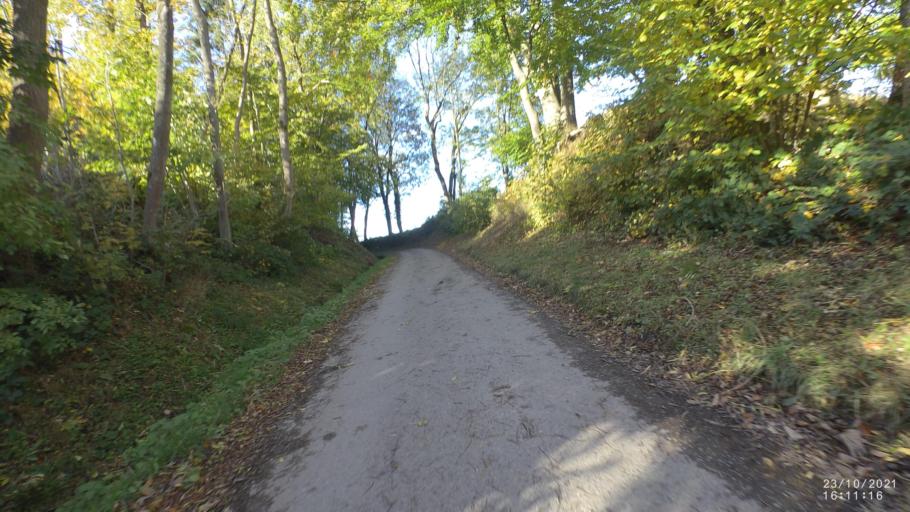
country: DE
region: North Rhine-Westphalia
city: Balve
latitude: 51.3733
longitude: 7.8387
